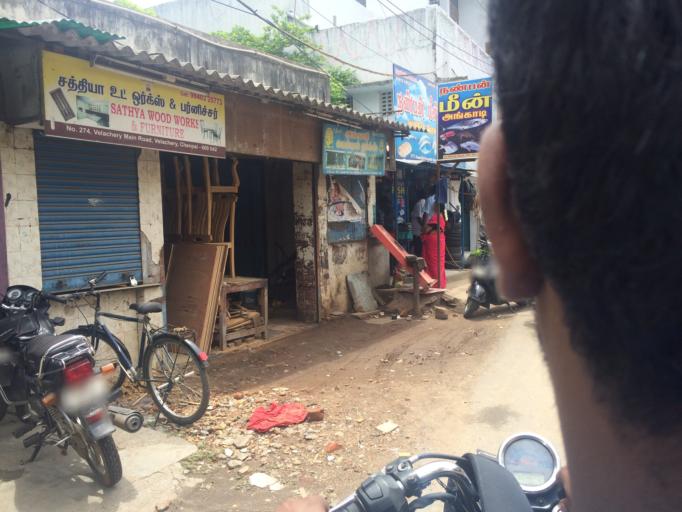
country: IN
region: Tamil Nadu
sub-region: Kancheepuram
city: Alandur
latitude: 12.9844
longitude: 80.2228
